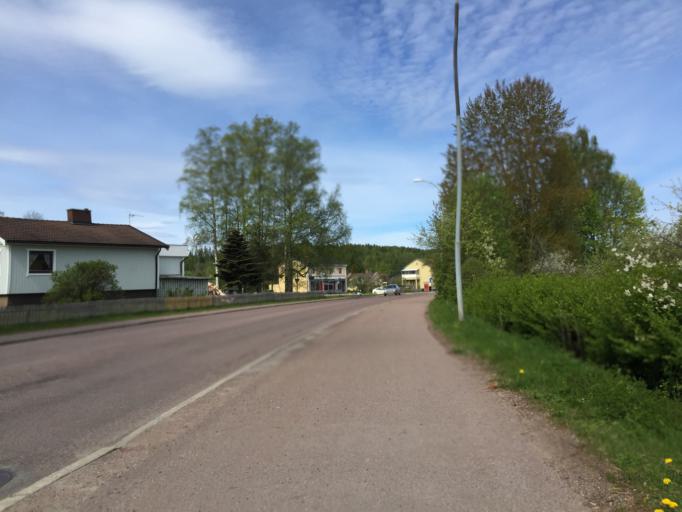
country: SE
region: Dalarna
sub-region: Ludvika Kommun
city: Ludvika
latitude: 60.1330
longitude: 15.1730
